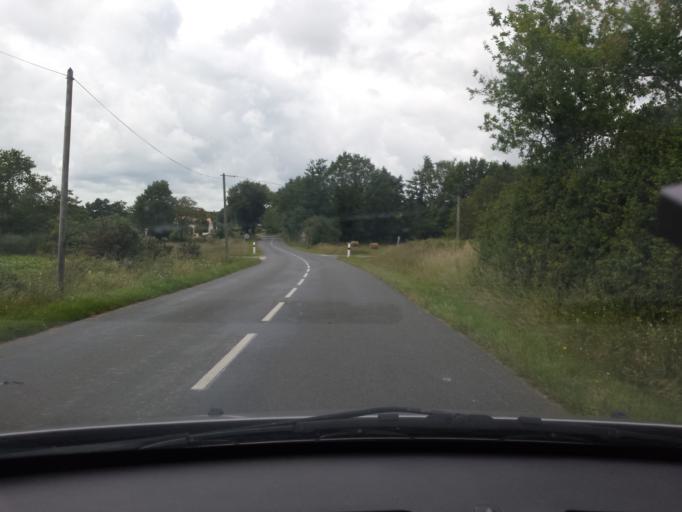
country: FR
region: Pays de la Loire
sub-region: Departement de la Vendee
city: Beaulieu-sous-la-Roche
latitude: 46.6700
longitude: -1.5961
